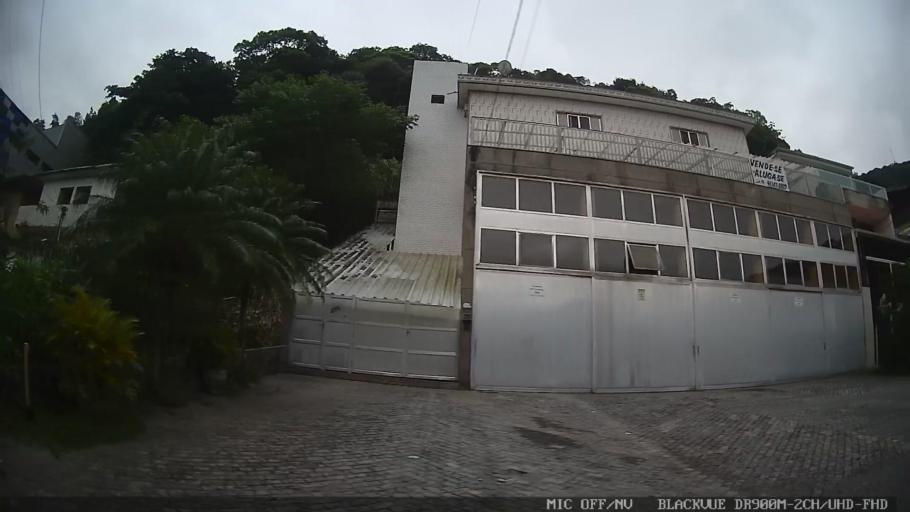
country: BR
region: Sao Paulo
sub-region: Guaruja
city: Guaruja
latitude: -23.9894
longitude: -46.2556
